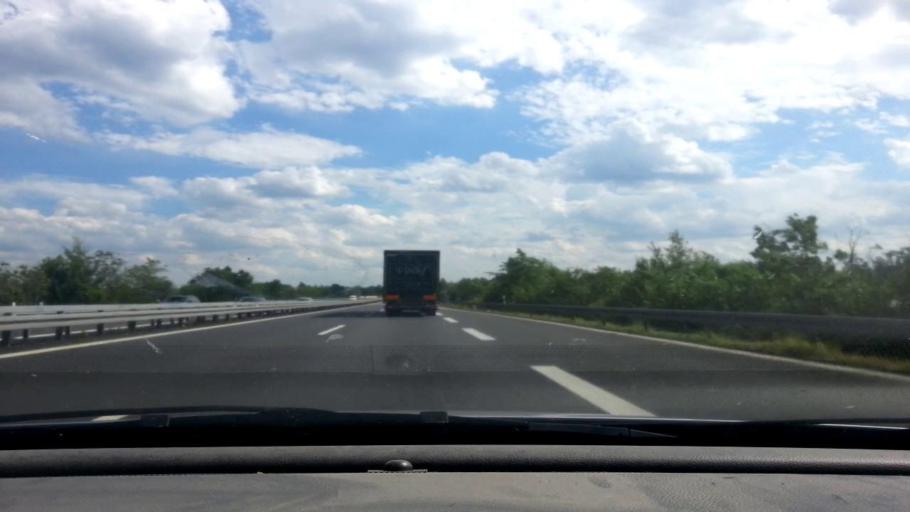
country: DE
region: Bavaria
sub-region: Upper Palatinate
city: Mitterteich
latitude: 49.9348
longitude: 12.2251
